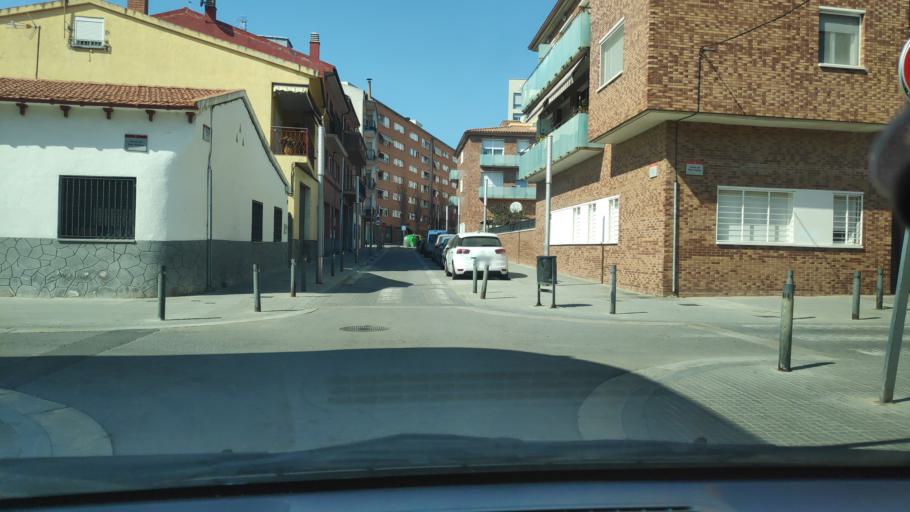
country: ES
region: Catalonia
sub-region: Provincia de Barcelona
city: Mollet del Valles
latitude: 41.5449
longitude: 2.2079
